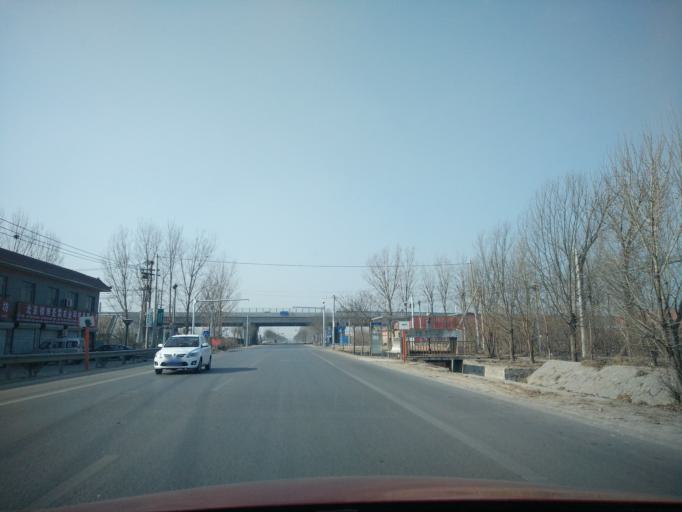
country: CN
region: Beijing
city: Yinghai
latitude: 39.7066
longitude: 116.4485
